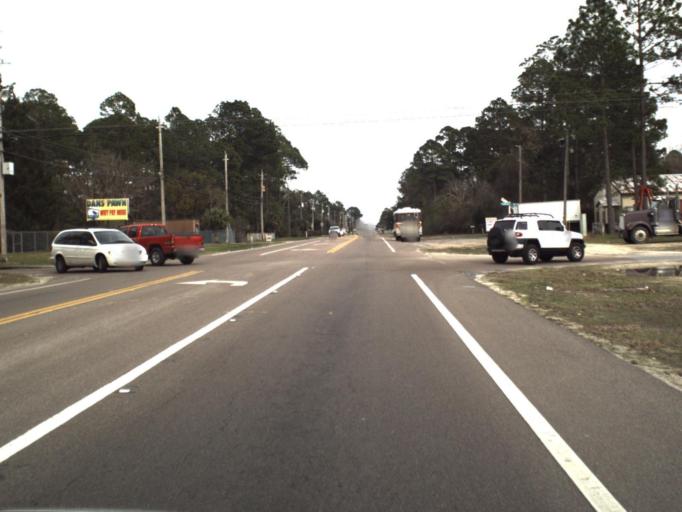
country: US
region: Florida
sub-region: Bay County
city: Callaway
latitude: 30.1529
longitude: -85.5833
